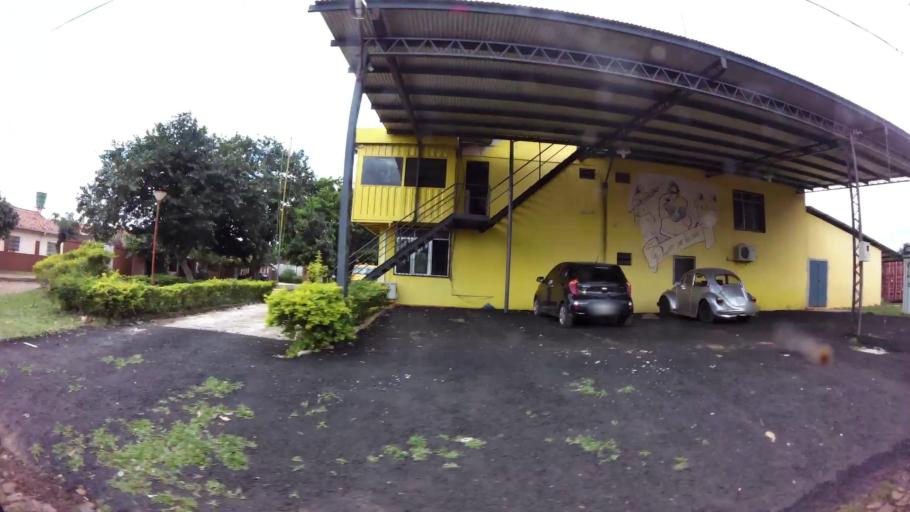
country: PY
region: Central
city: San Lorenzo
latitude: -25.2720
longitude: -57.5030
